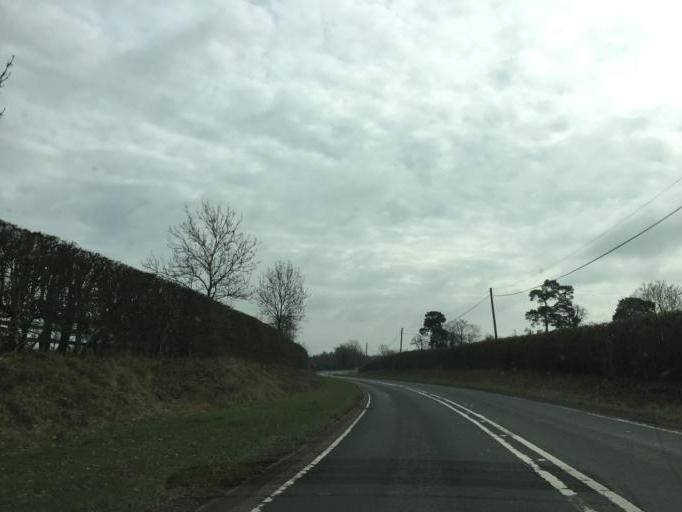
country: GB
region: England
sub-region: Warwickshire
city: Henley in Arden
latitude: 52.2932
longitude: -1.8265
